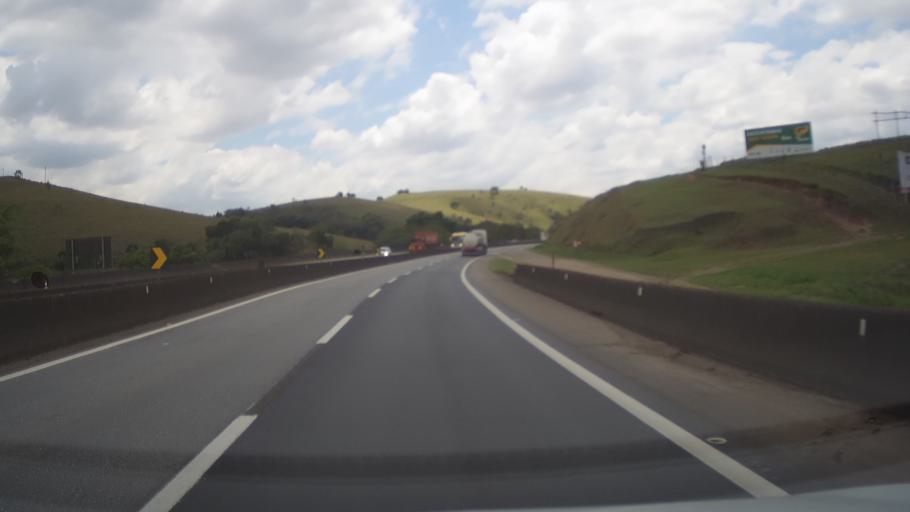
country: BR
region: Minas Gerais
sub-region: Tres Coracoes
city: Tres Coracoes
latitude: -21.7107
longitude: -45.3756
